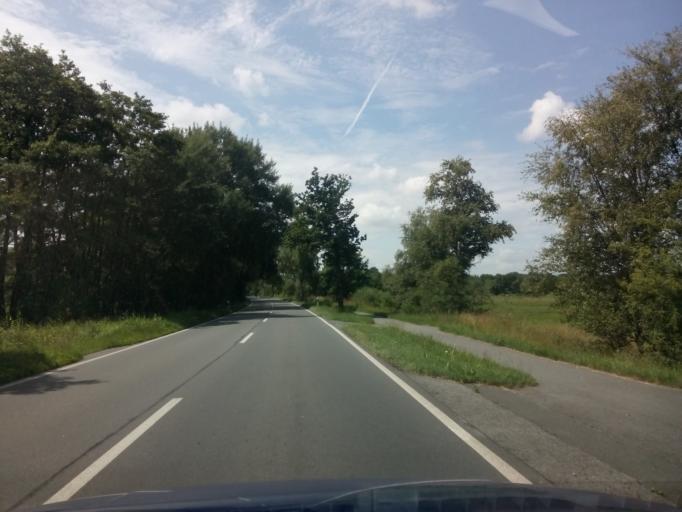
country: DE
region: Lower Saxony
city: Osterholz-Scharmbeck
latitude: 53.2522
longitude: 8.8316
